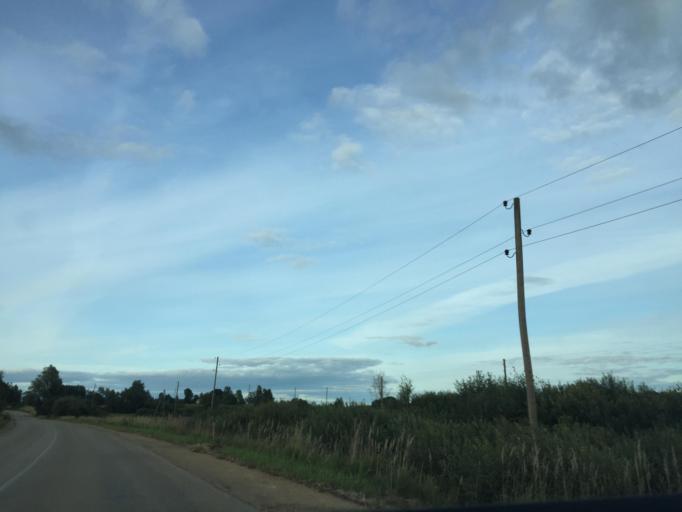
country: LV
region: Viesite
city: Viesite
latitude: 56.3013
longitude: 25.4372
